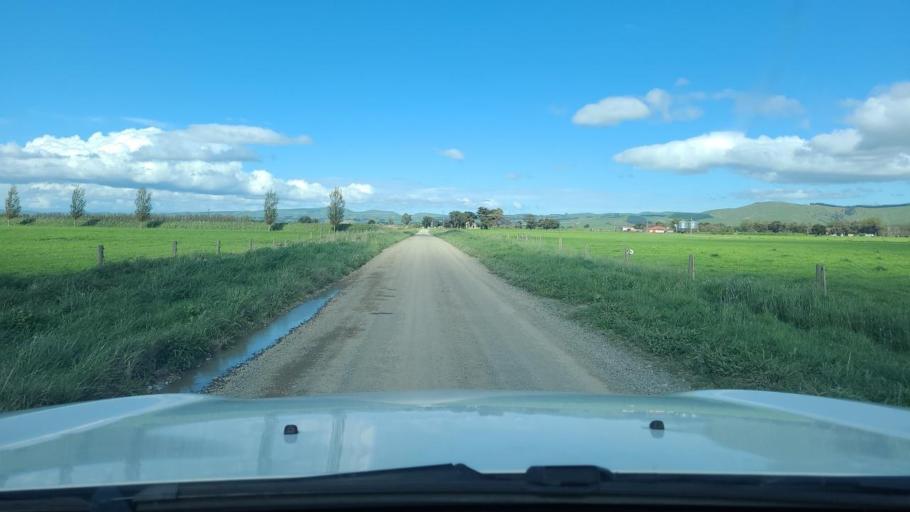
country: NZ
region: Wellington
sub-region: South Wairarapa District
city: Waipawa
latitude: -41.2422
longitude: 175.3492
